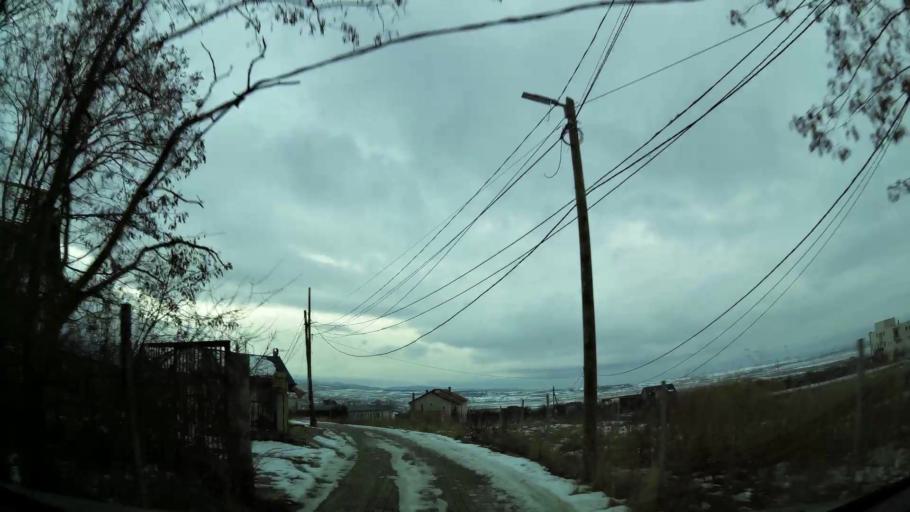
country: XK
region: Pristina
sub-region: Komuna e Prishtines
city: Pristina
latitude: 42.6240
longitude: 21.1633
